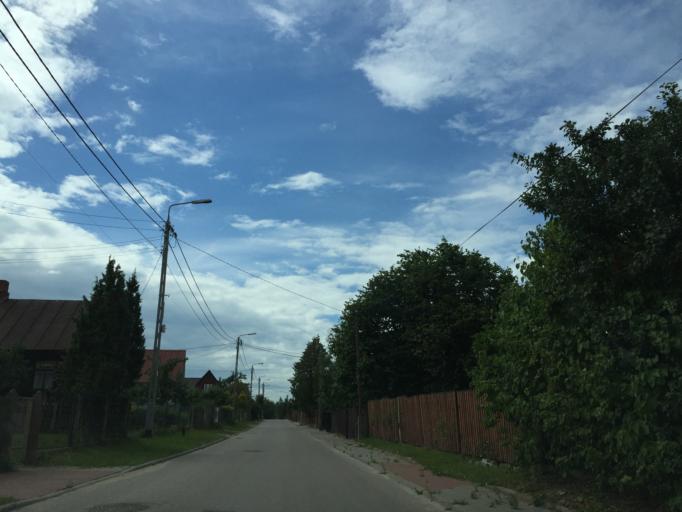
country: PL
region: Podlasie
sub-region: Powiat bielski
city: Bielsk Podlaski
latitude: 52.7442
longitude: 23.1897
